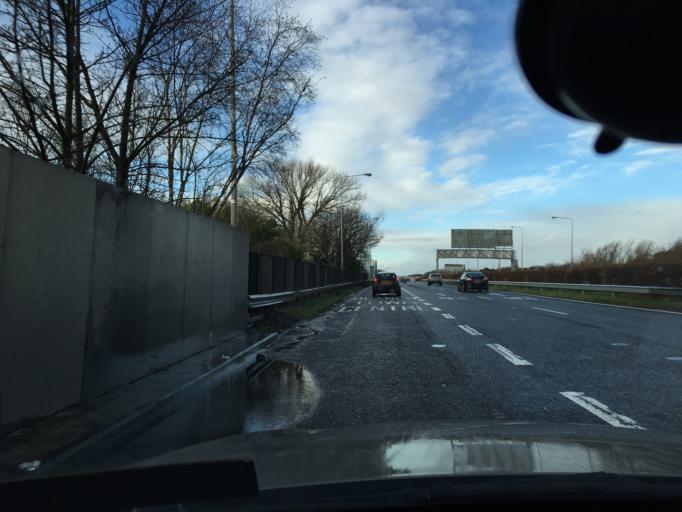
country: IE
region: Leinster
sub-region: Fingal County
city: Blanchardstown
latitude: 53.3875
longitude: -6.3736
